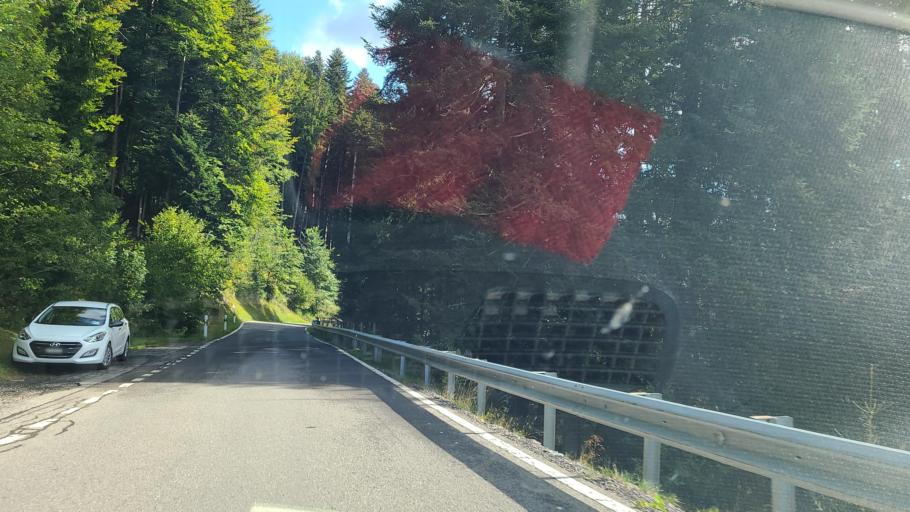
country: CH
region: Schwyz
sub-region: Bezirk March
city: Vorderthal
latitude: 47.1303
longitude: 8.8668
